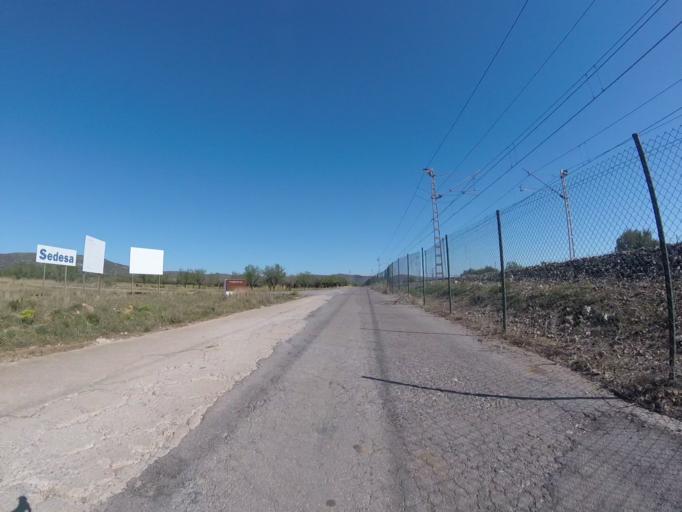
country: ES
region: Valencia
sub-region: Provincia de Castello
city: Alcala de Xivert
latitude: 40.3141
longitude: 0.2324
